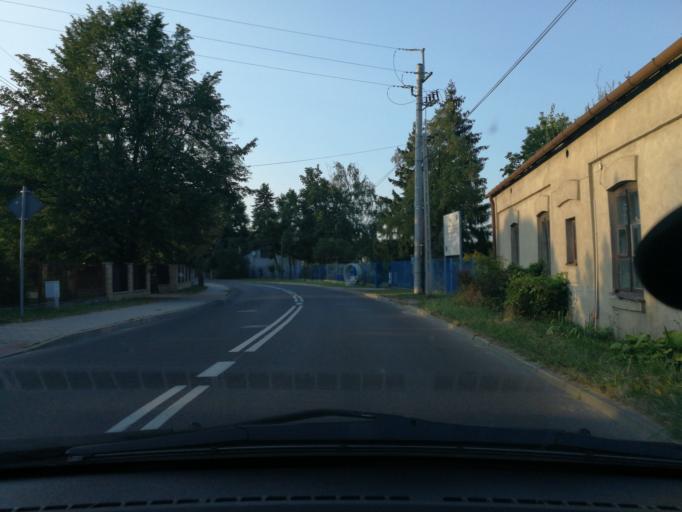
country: PL
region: Lodz Voivodeship
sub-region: Skierniewice
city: Skierniewice
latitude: 51.9675
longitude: 20.1358
